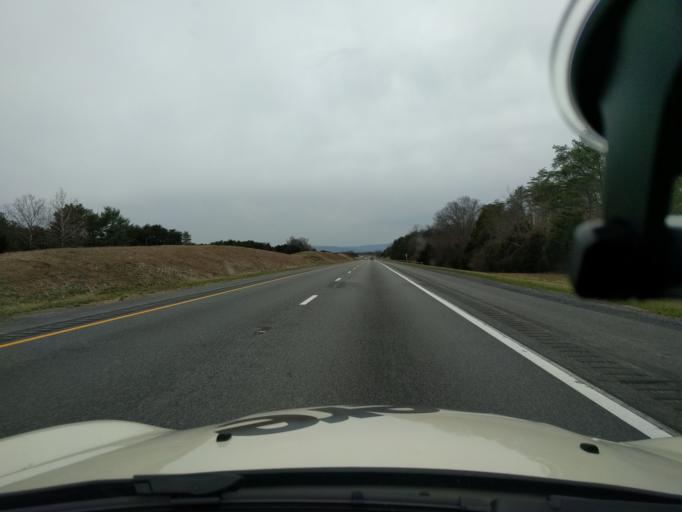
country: US
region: Virginia
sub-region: Frederick County
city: Middletown
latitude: 38.9845
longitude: -78.2335
